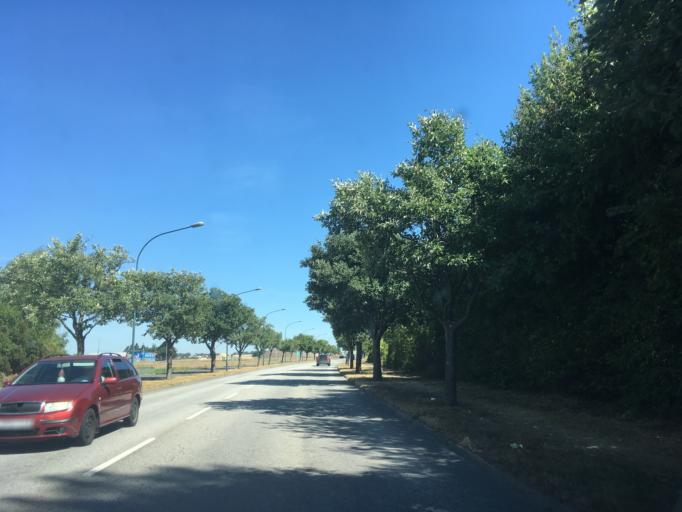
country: SE
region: Skane
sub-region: Trelleborgs Kommun
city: Trelleborg
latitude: 55.3806
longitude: 13.1245
